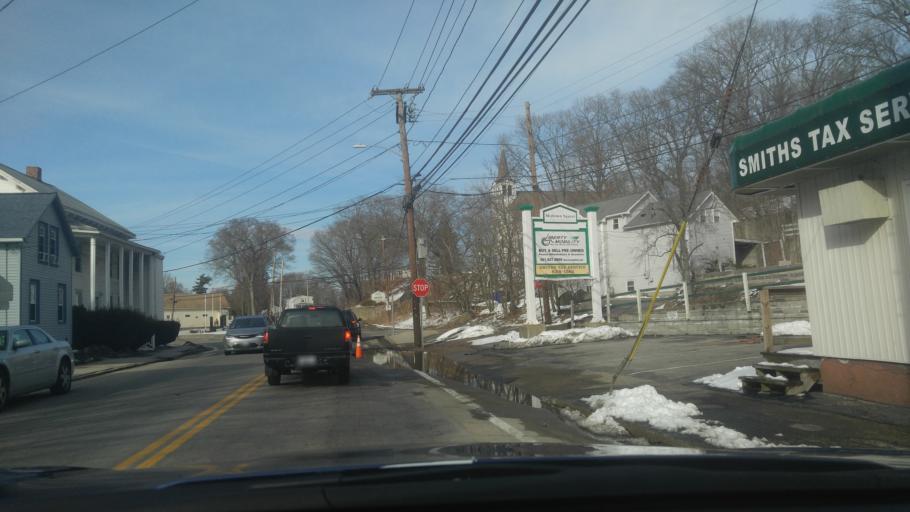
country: US
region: Rhode Island
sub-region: Kent County
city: West Warwick
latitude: 41.6916
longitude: -71.5210
